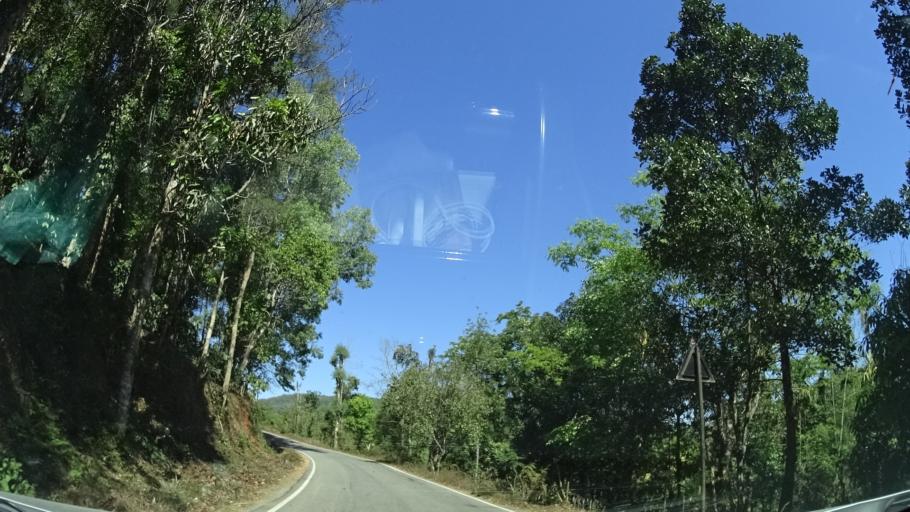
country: IN
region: Karnataka
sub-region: Chikmagalur
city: Sringeri
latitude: 13.2205
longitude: 75.3479
